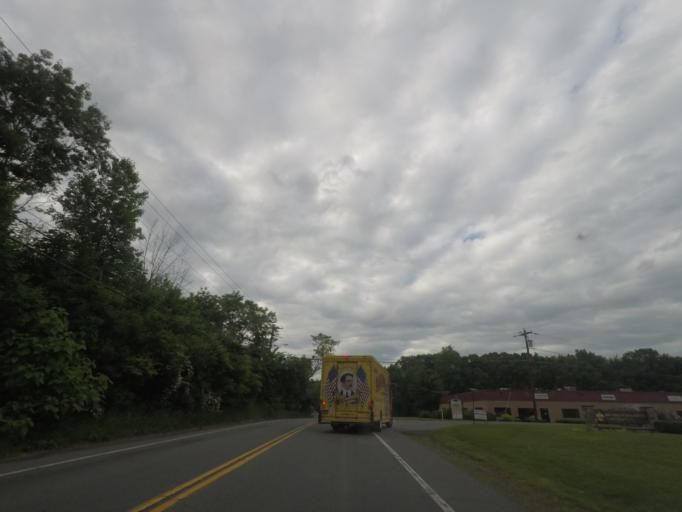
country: US
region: New York
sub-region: Orange County
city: Gardnertown
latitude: 41.5426
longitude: -74.0618
